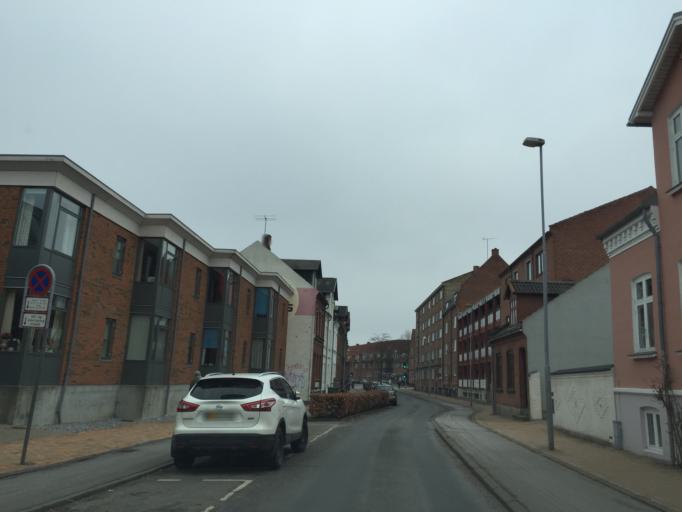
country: DK
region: South Denmark
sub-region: Odense Kommune
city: Odense
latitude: 55.3937
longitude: 10.4021
